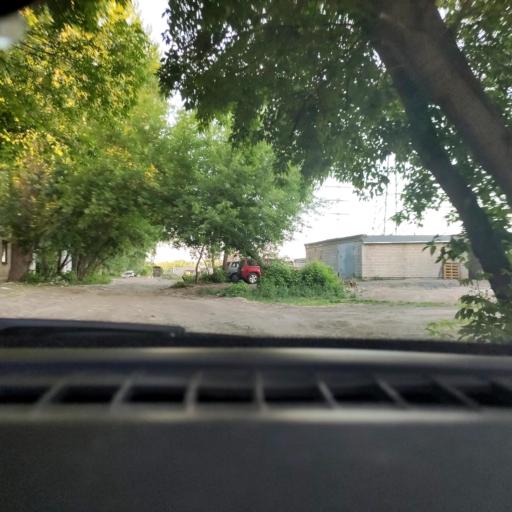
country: RU
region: Samara
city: Petra-Dubrava
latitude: 53.2980
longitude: 50.2906
